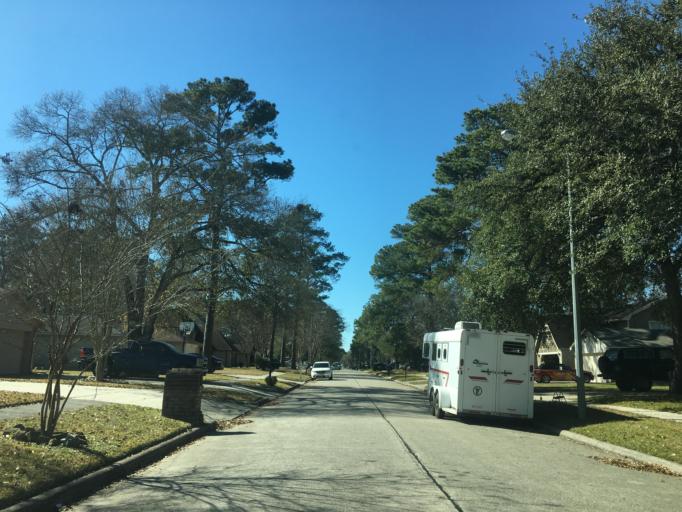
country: US
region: Texas
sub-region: Harris County
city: Spring
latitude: 30.0890
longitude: -95.4668
